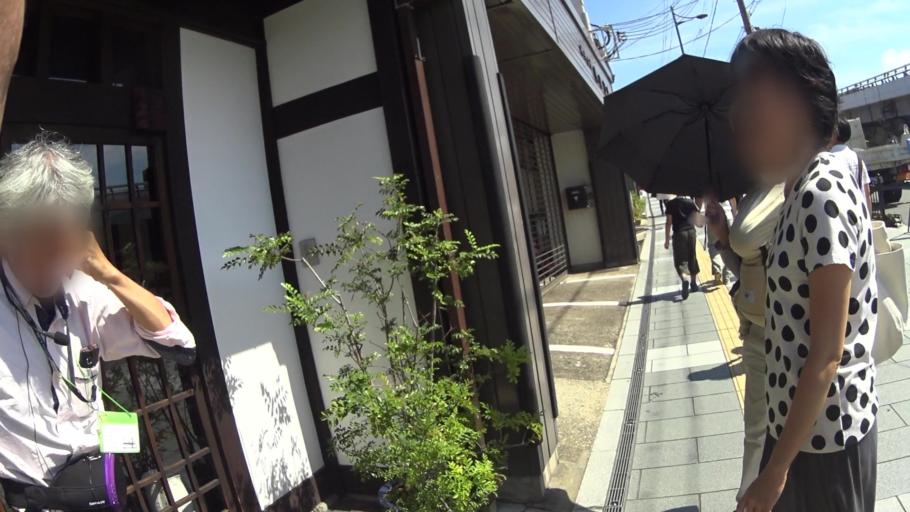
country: JP
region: Kyoto
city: Kyoto
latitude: 34.9947
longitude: 135.7747
